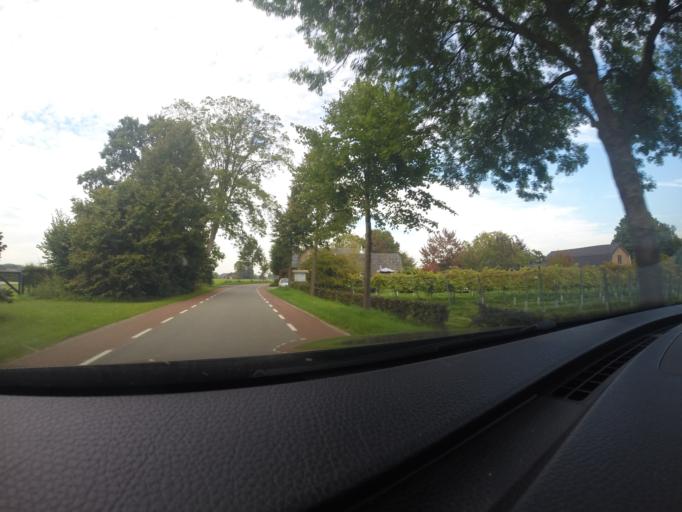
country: NL
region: Gelderland
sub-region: Gemeente Bronckhorst
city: Hengelo
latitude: 52.0214
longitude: 6.2937
